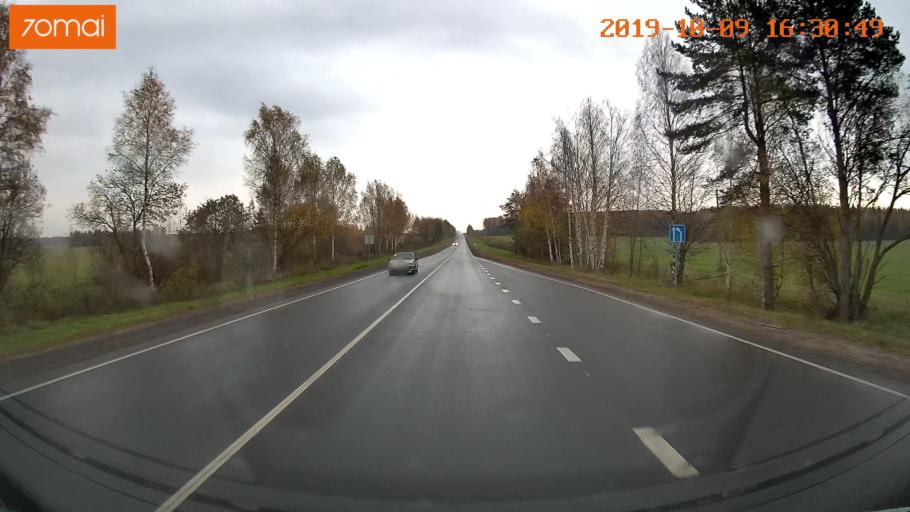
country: RU
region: Kostroma
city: Oktyabr'skiy
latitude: 57.6143
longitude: 40.9445
